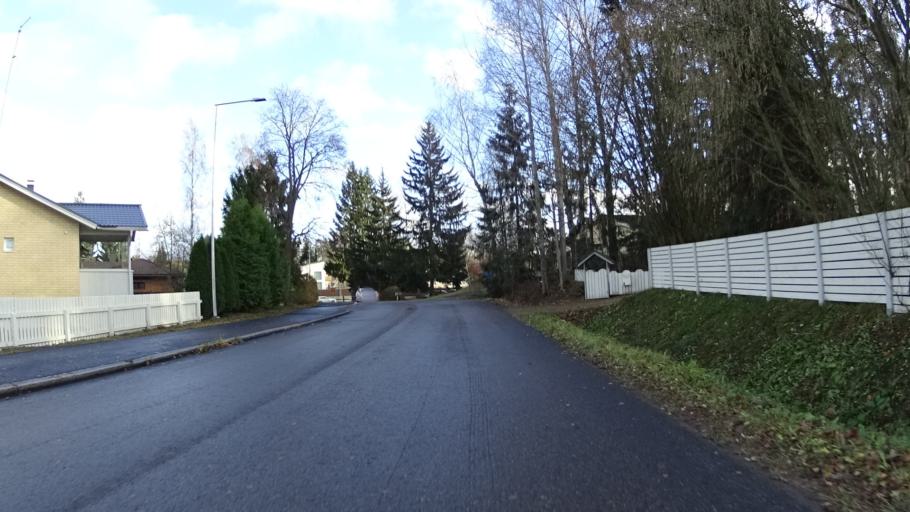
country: FI
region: Uusimaa
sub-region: Helsinki
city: Vantaa
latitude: 60.3033
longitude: 25.0309
